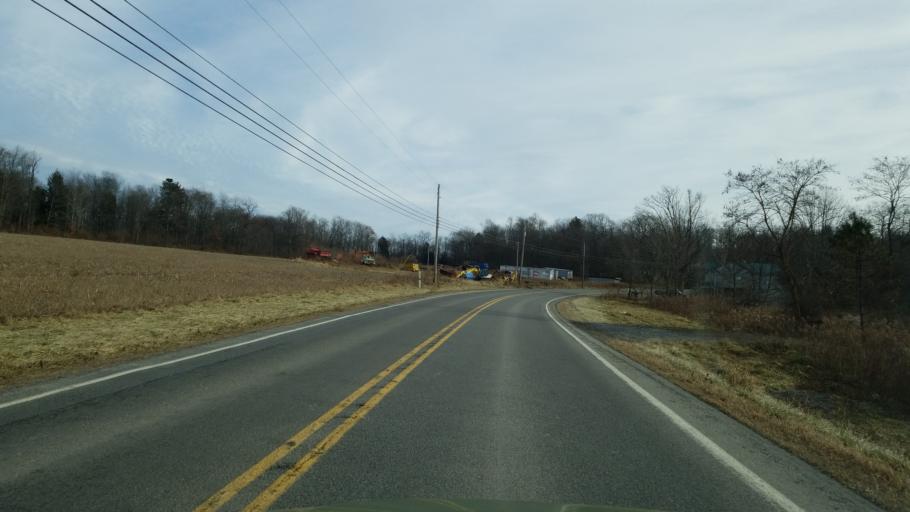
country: US
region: Pennsylvania
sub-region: Indiana County
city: Johnsonburg
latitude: 40.9200
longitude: -78.8512
